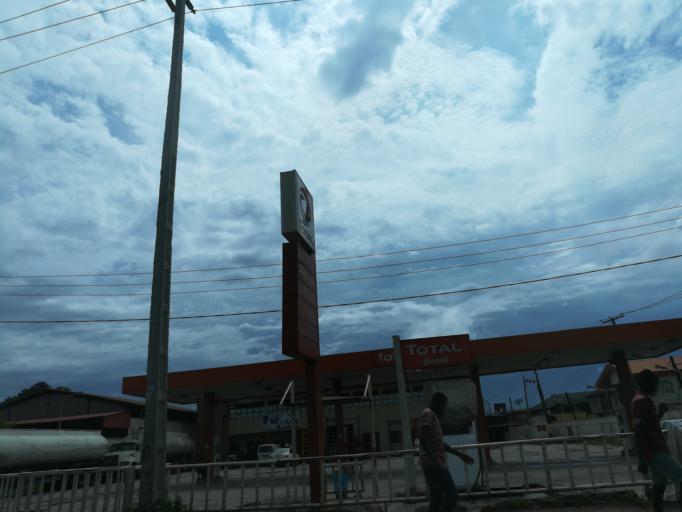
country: NG
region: Lagos
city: Agege
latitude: 6.6082
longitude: 3.3305
